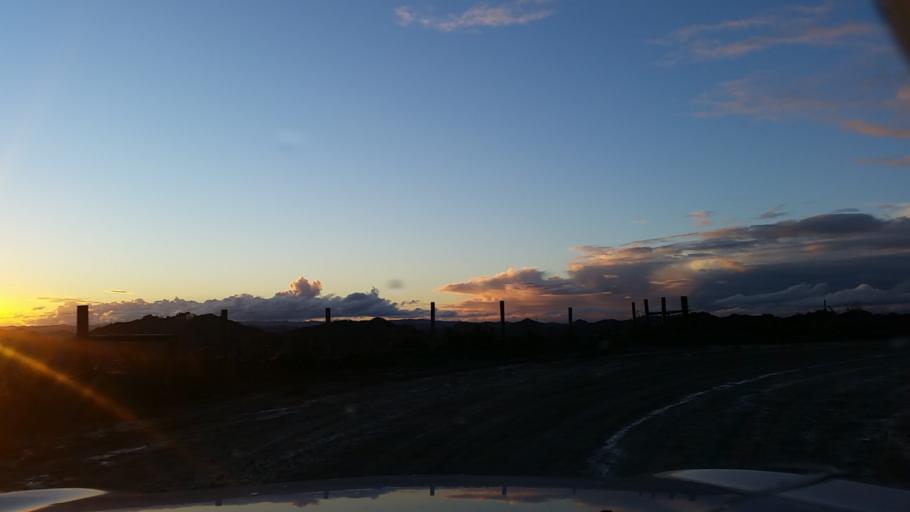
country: NZ
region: Manawatu-Wanganui
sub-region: Wanganui District
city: Wanganui
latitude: -39.7639
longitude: 174.8758
